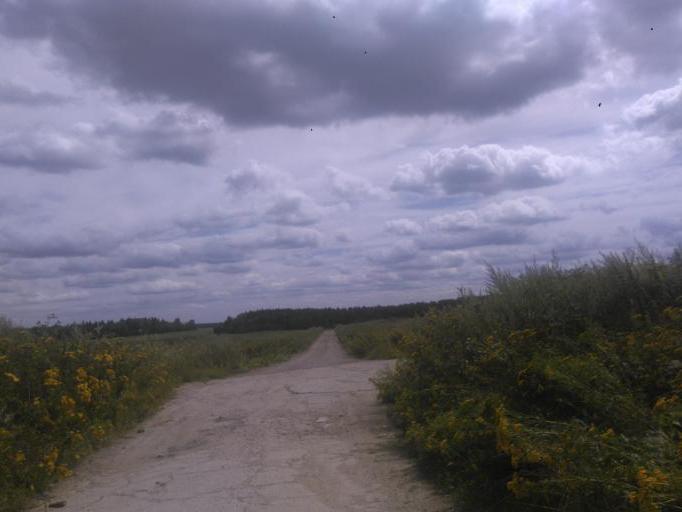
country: RU
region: Moskovskaya
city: Solnechnogorsk
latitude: 56.1447
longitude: 36.9218
